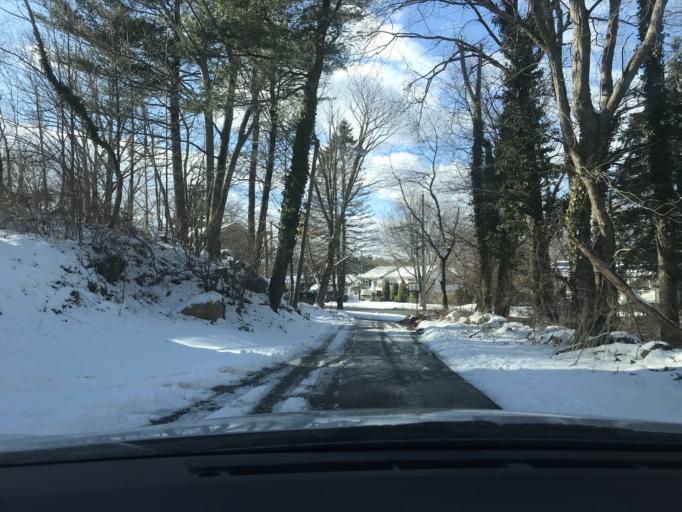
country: US
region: Massachusetts
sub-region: Essex County
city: Saugus
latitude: 42.4899
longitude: -71.0127
